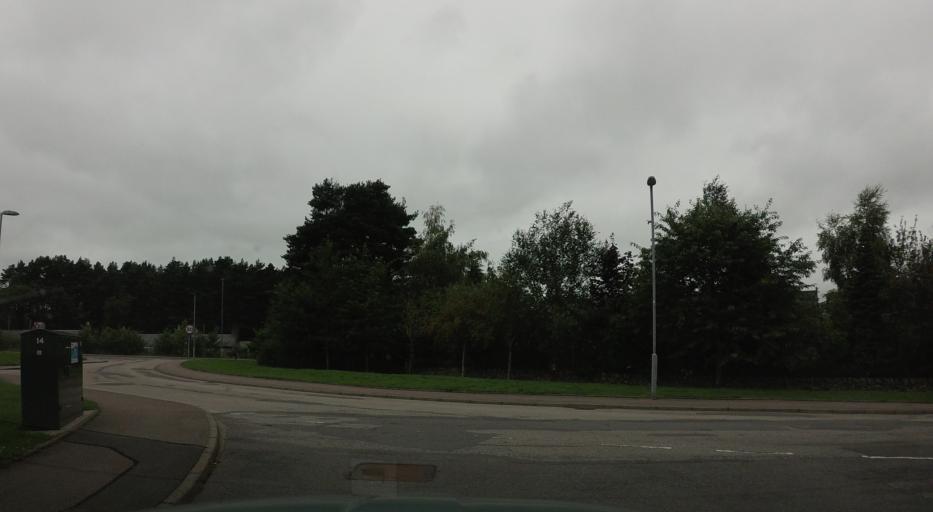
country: GB
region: Scotland
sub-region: Aberdeenshire
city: Banchory
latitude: 57.0591
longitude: -2.4913
